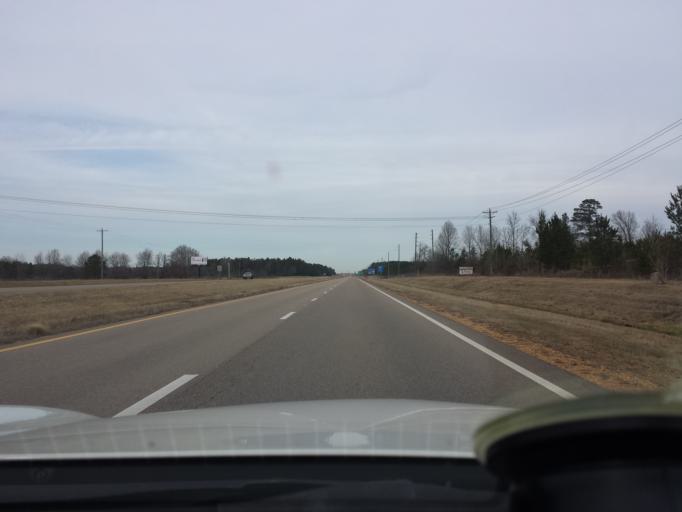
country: US
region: Mississippi
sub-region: Oktibbeha County
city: Starkville
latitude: 33.4187
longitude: -88.8538
